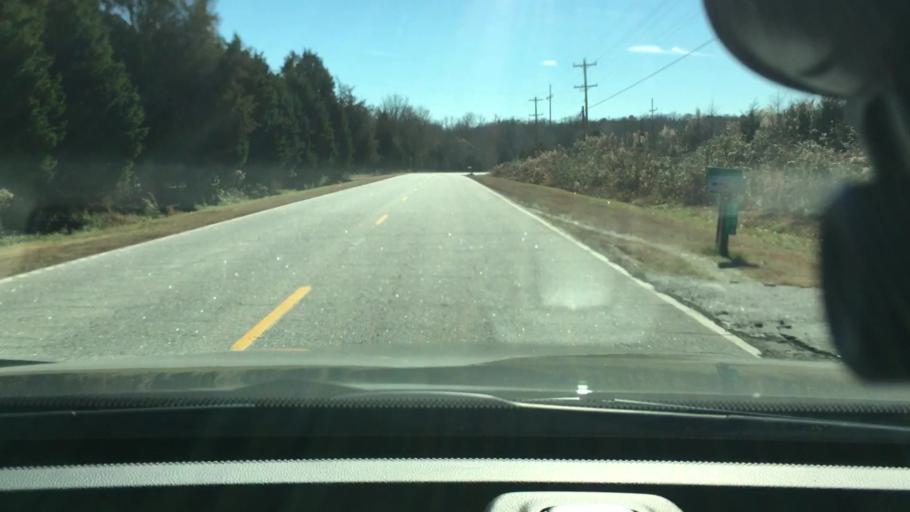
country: US
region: South Carolina
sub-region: Cherokee County
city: Gaffney
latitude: 34.9959
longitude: -81.6915
